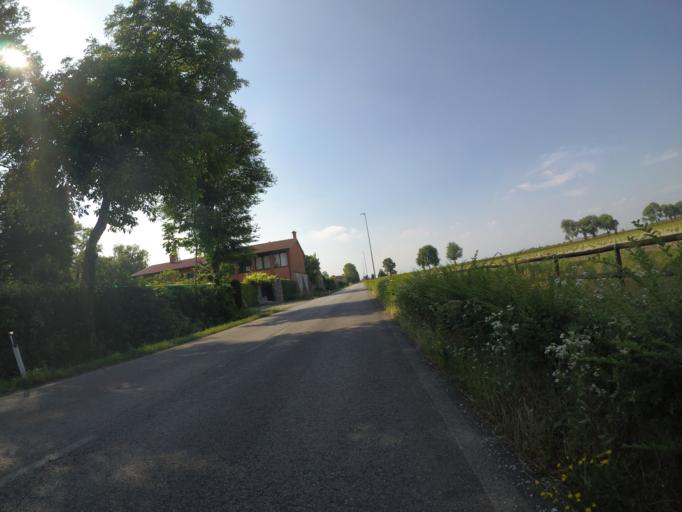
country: IT
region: Friuli Venezia Giulia
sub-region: Provincia di Udine
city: Camino al Tagliamento
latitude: 45.9292
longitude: 12.9602
